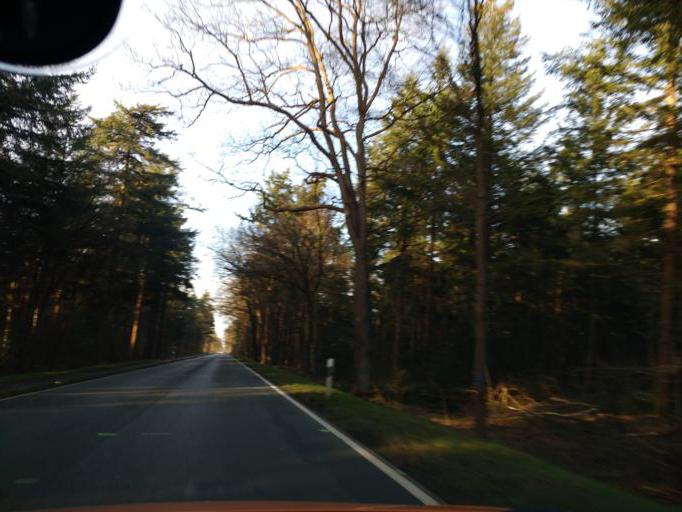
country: DE
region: Lower Saxony
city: Hatten
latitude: 53.0940
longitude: 8.3258
